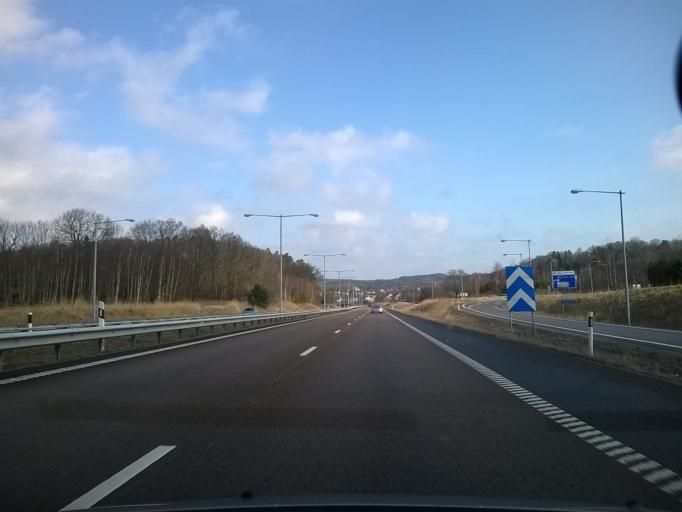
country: SE
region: Vaestra Goetaland
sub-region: Uddevalla Kommun
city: Ljungskile
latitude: 58.2136
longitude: 11.9148
